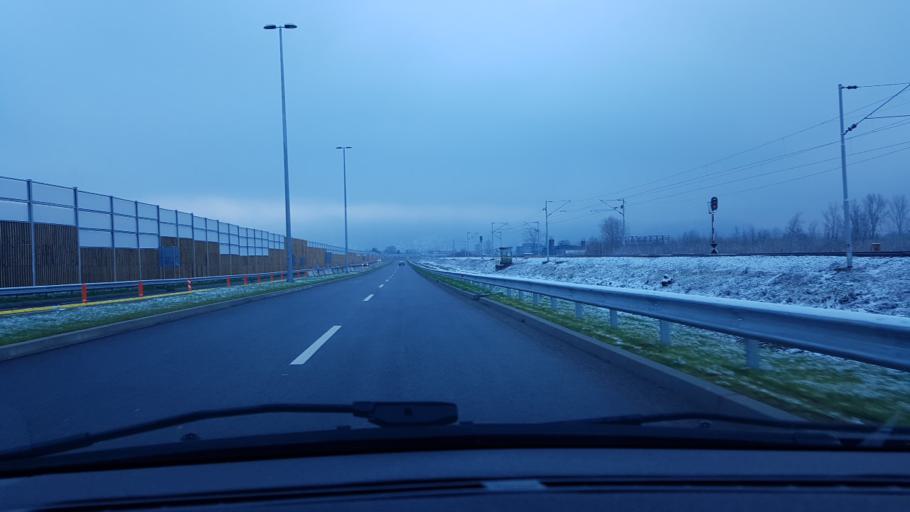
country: HR
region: Zagrebacka
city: Zapresic
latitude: 45.8547
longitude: 15.7965
